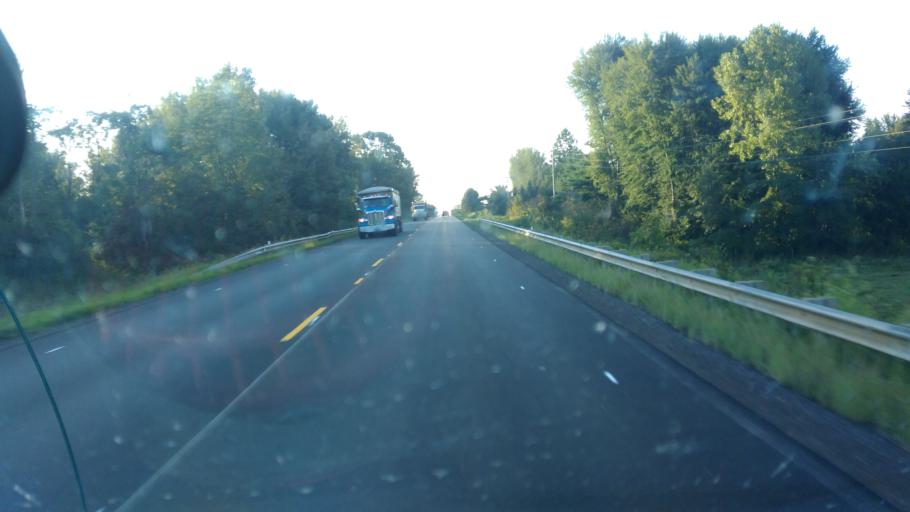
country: US
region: Ohio
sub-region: Morrow County
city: Mount Gilead
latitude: 40.5197
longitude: -82.7502
